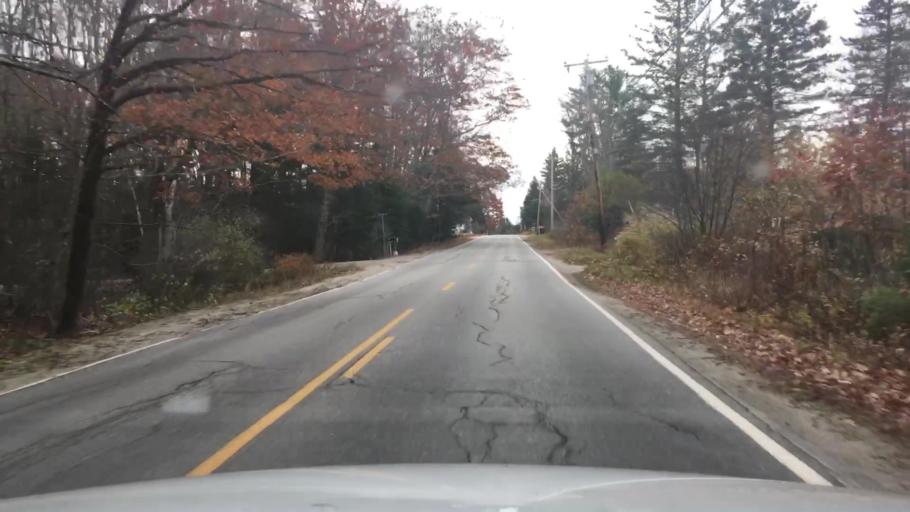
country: US
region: Maine
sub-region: Hancock County
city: Sedgwick
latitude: 44.3661
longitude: -68.5531
